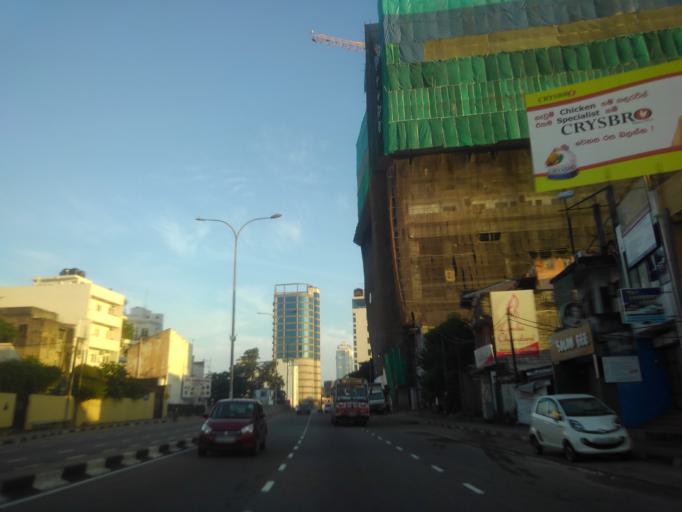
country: LK
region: Western
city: Pita Kotte
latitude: 6.8820
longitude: 79.8763
